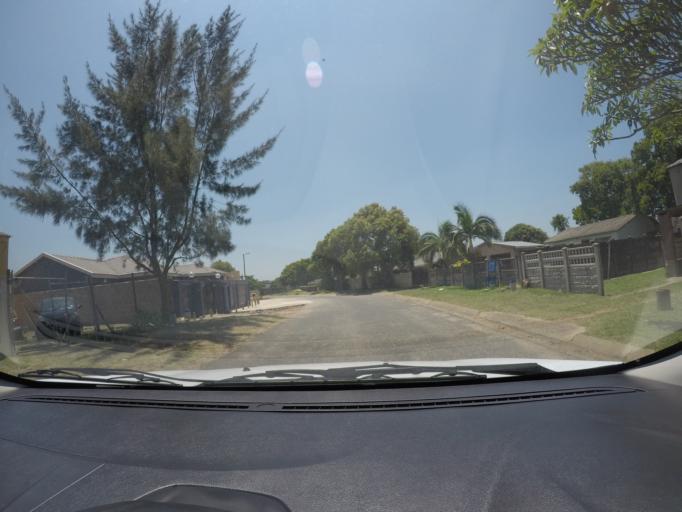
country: ZA
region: KwaZulu-Natal
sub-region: uThungulu District Municipality
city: eSikhawini
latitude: -28.8785
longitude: 31.9059
